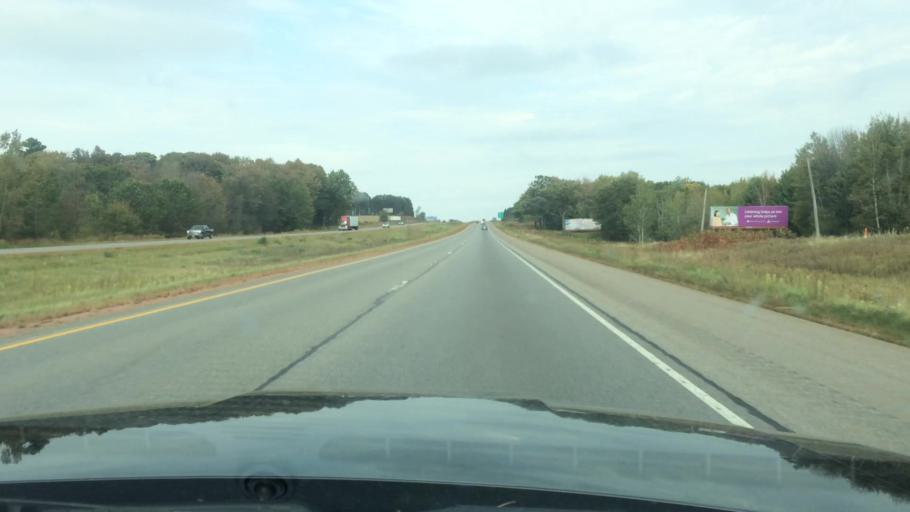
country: US
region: Wisconsin
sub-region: Marathon County
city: Mosinee
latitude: 44.7611
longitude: -89.6798
